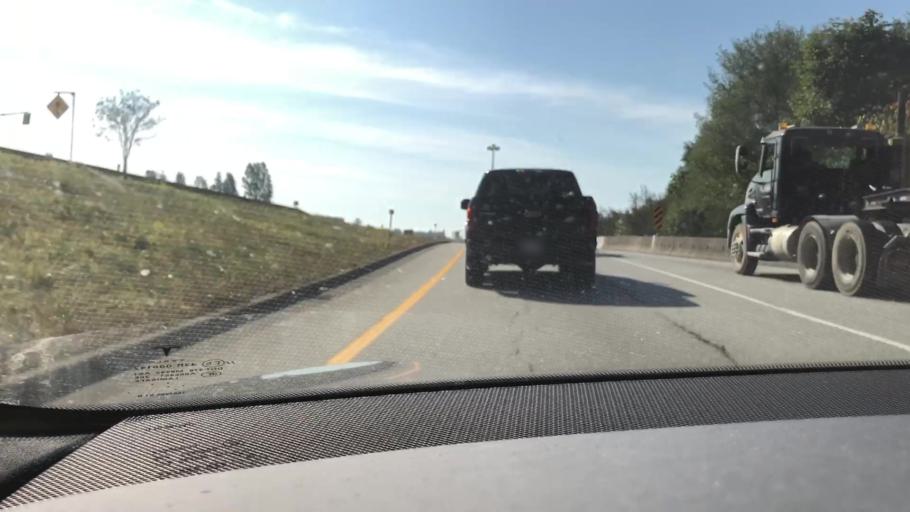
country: CA
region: British Columbia
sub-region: Fraser Valley Regional District
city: North Vancouver
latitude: 49.2878
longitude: -123.0321
